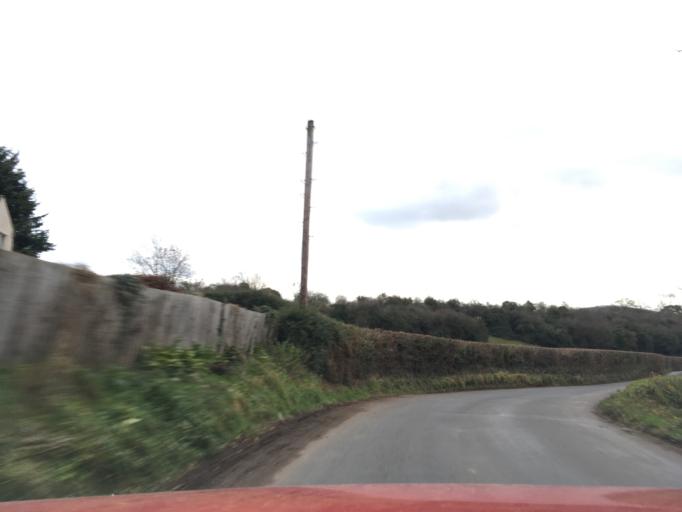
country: GB
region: Wales
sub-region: Newport
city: Llanvaches
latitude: 51.6138
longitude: -2.8291
